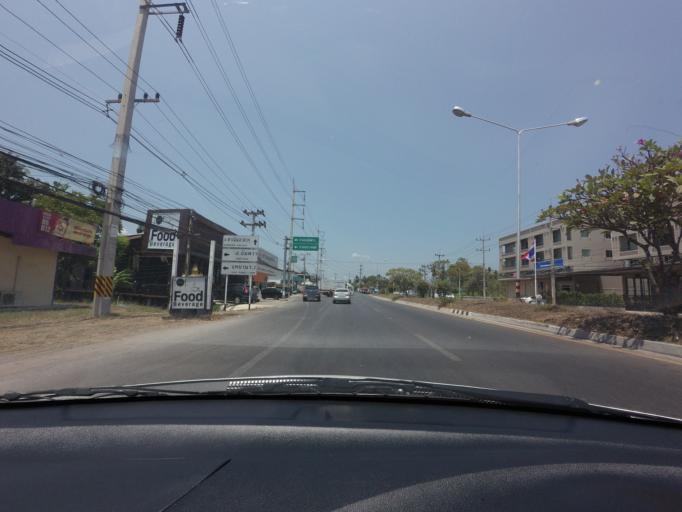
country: TH
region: Samut Songkhram
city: Amphawa
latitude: 13.4215
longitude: 99.9630
